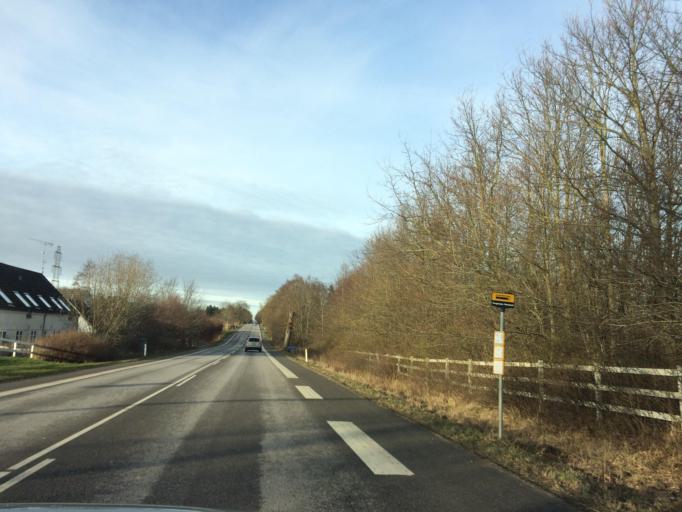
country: DK
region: Capital Region
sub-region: Fredensborg Kommune
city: Fredensborg
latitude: 55.9332
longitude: 12.4367
